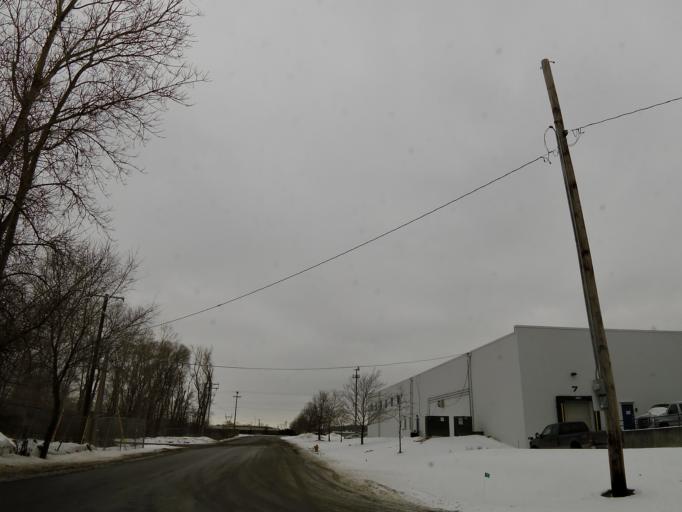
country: US
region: Minnesota
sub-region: Dakota County
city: South Saint Paul
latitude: 44.8767
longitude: -93.0283
